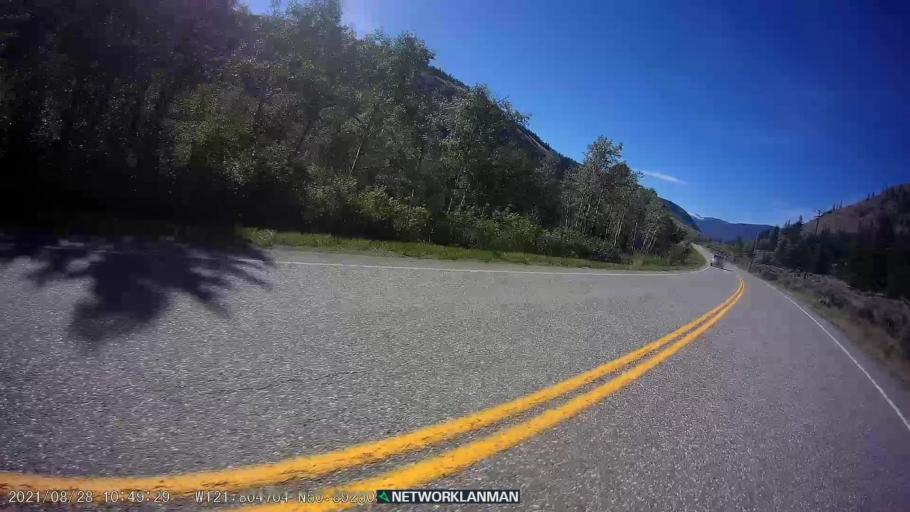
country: CA
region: British Columbia
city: Lillooet
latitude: 50.8945
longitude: -121.8037
